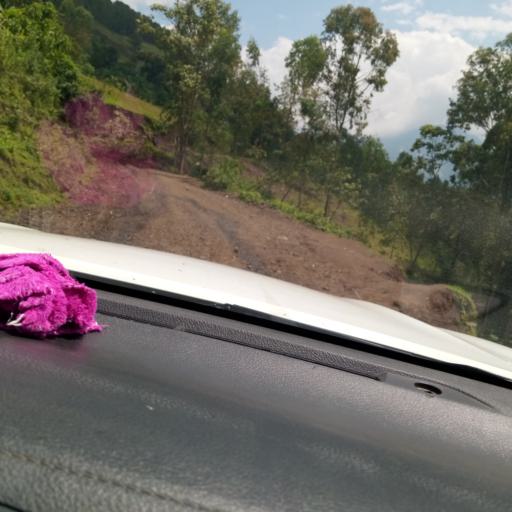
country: ET
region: Southern Nations, Nationalities, and People's Region
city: Arba Minch'
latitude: 6.3118
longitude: 37.3718
